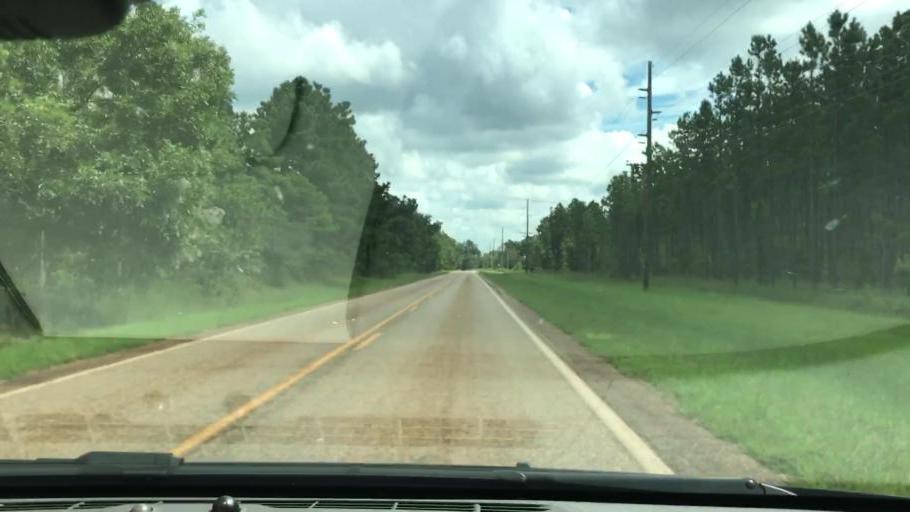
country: US
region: Georgia
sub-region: Stewart County
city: Lumpkin
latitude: 32.0676
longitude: -84.8900
